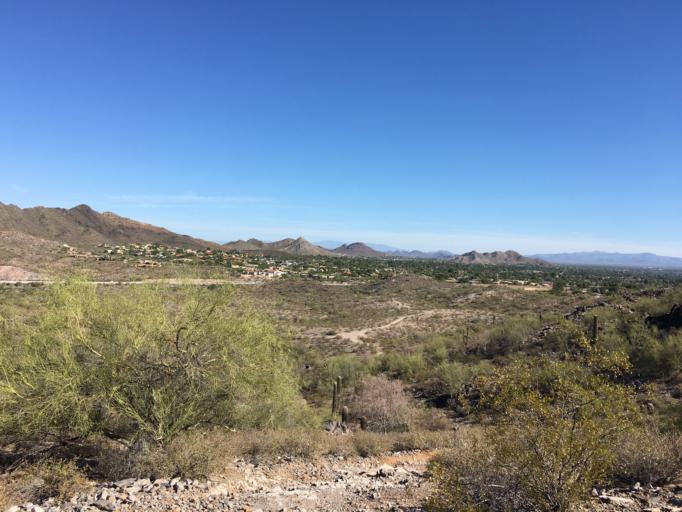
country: US
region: Arizona
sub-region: Maricopa County
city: Paradise Valley
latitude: 33.5628
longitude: -112.0212
